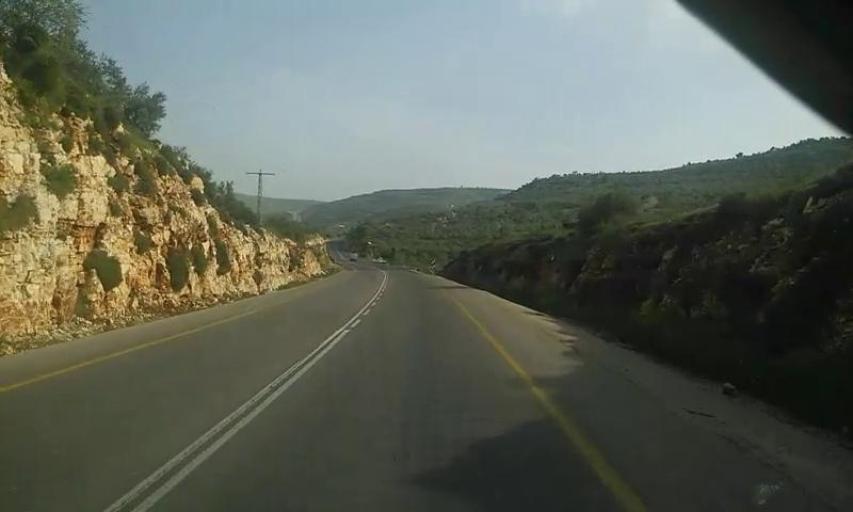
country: PS
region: West Bank
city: Jit
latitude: 32.2250
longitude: 35.1736
